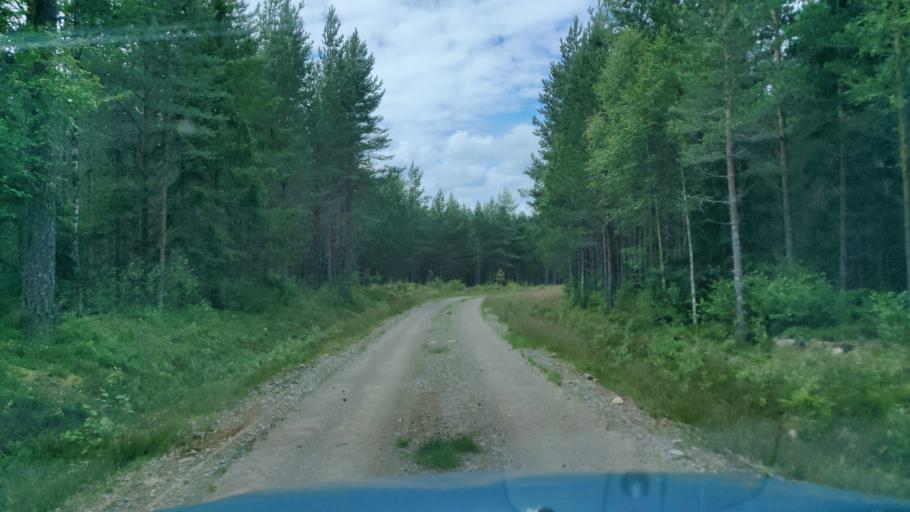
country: SE
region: Vaermland
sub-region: Hagfors Kommun
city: Hagfors
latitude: 59.9512
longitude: 13.5917
